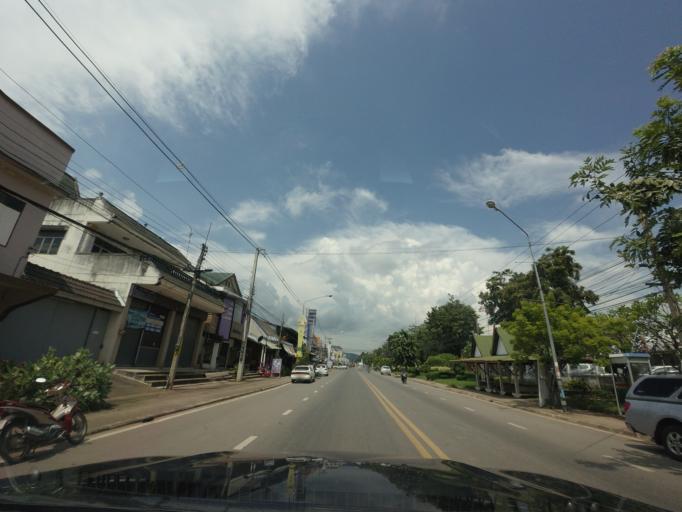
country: TH
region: Khon Kaen
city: Phu Wiang
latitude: 16.6514
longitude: 102.3798
